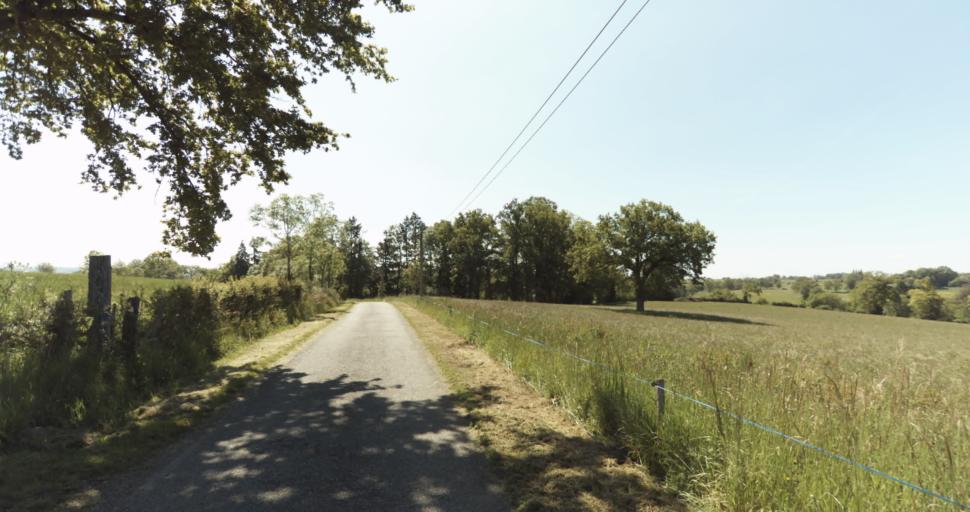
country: FR
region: Limousin
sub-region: Departement de la Haute-Vienne
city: Le Vigen
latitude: 45.7335
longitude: 1.2929
